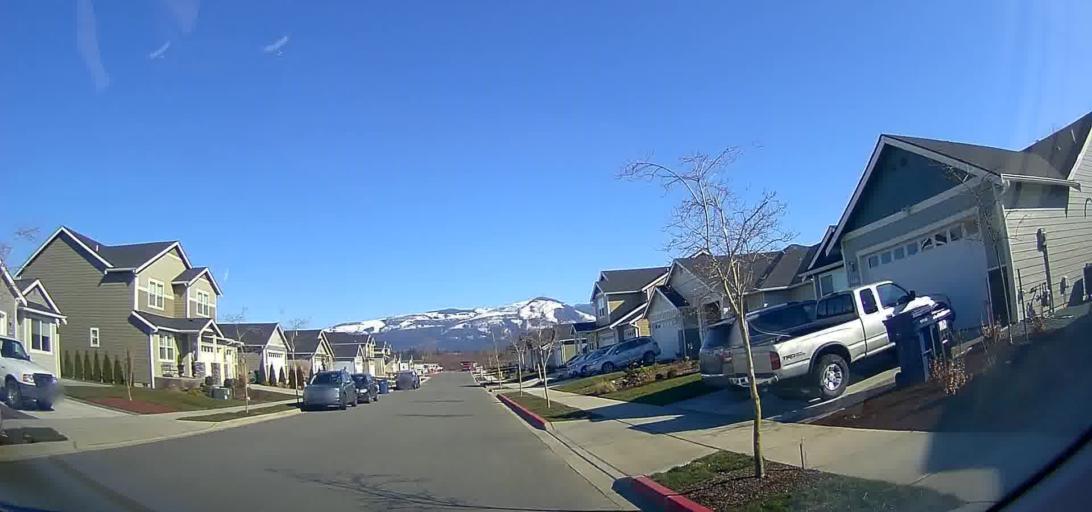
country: US
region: Washington
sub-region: Skagit County
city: Mount Vernon
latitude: 48.4384
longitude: -122.2887
